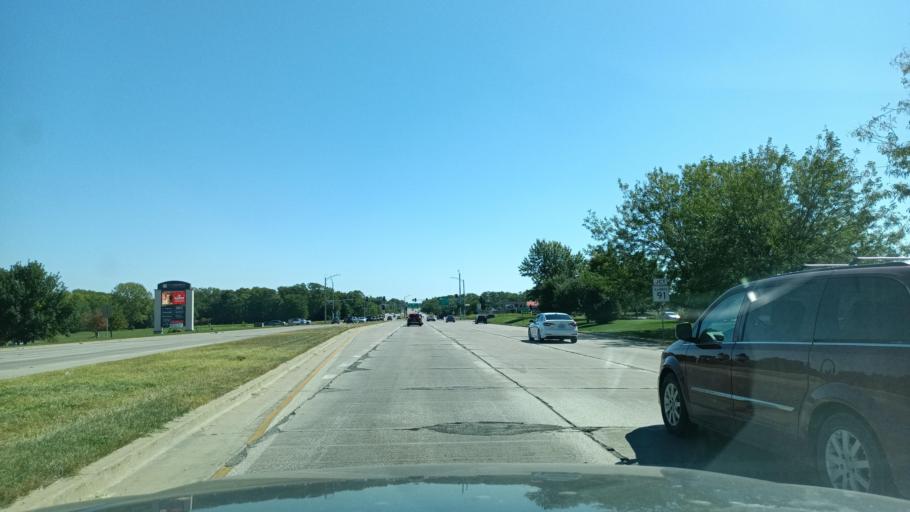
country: US
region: Illinois
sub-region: Peoria County
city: Dunlap
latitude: 40.7769
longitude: -89.6764
